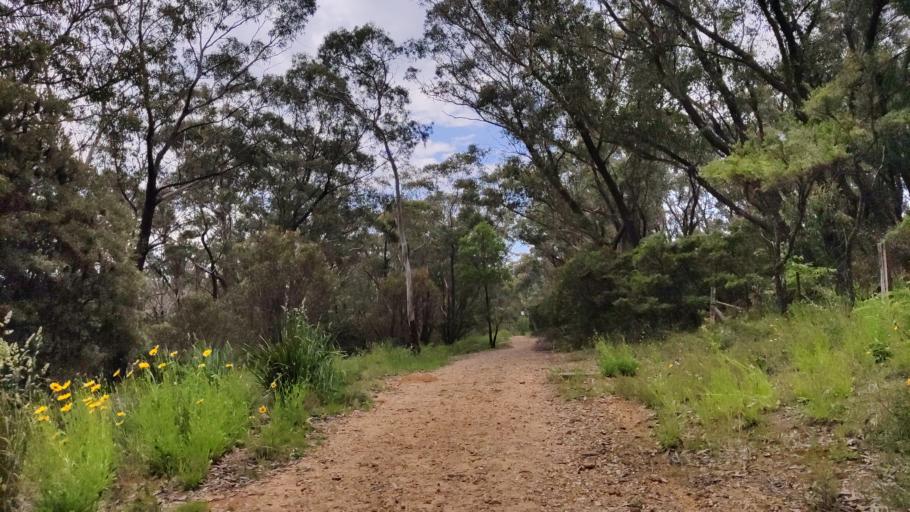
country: AU
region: New South Wales
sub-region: Blue Mountains Municipality
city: Leura
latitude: -33.7165
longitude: 150.3271
